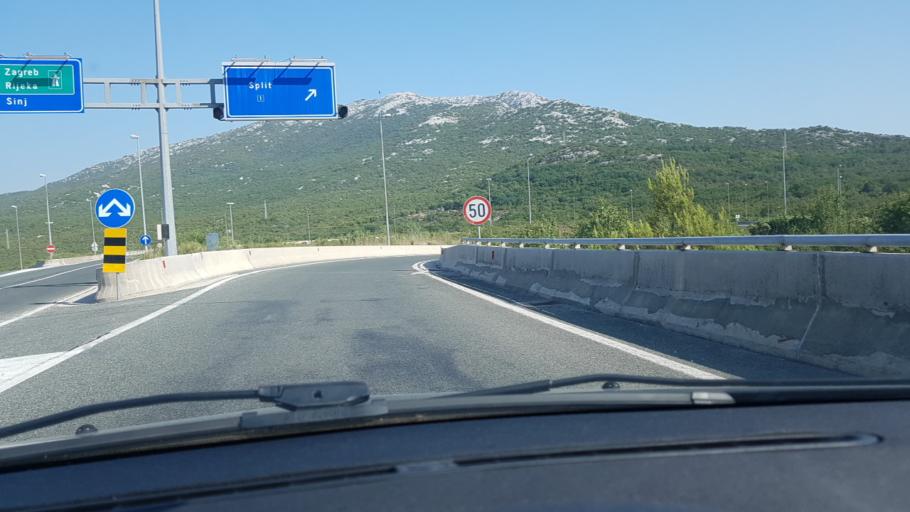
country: HR
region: Splitsko-Dalmatinska
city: Klis
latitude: 43.5762
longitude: 16.5374
